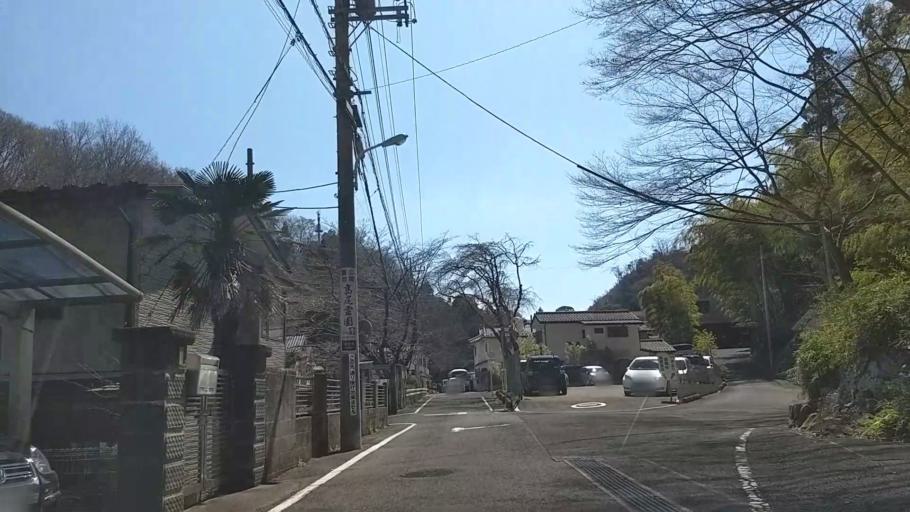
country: JP
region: Tokyo
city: Hachioji
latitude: 35.6349
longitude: 139.2763
